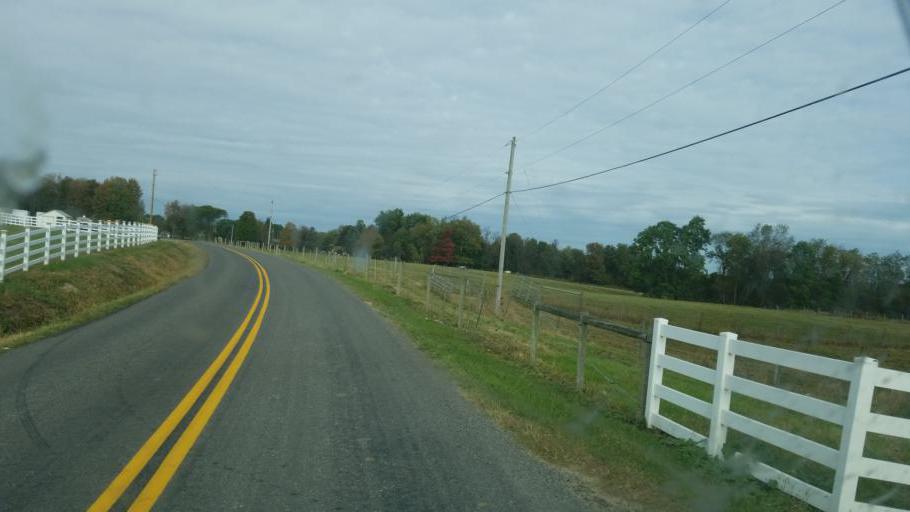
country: US
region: Pennsylvania
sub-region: Mercer County
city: Mercer
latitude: 41.3375
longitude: -80.2642
